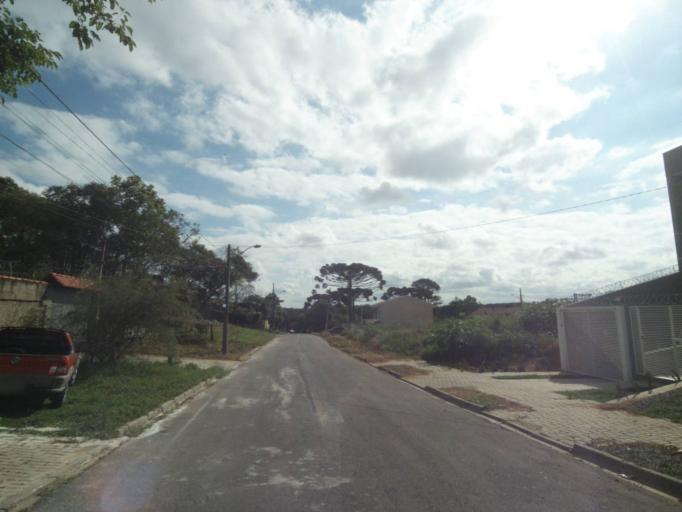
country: BR
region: Parana
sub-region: Curitiba
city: Curitiba
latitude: -25.3820
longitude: -49.2959
